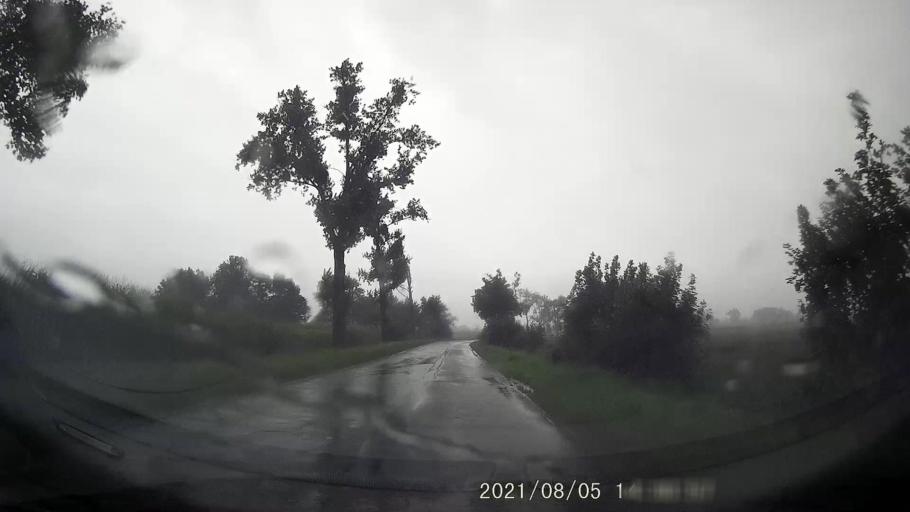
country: PL
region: Opole Voivodeship
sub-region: Powiat nyski
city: Korfantow
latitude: 50.4798
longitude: 17.5577
